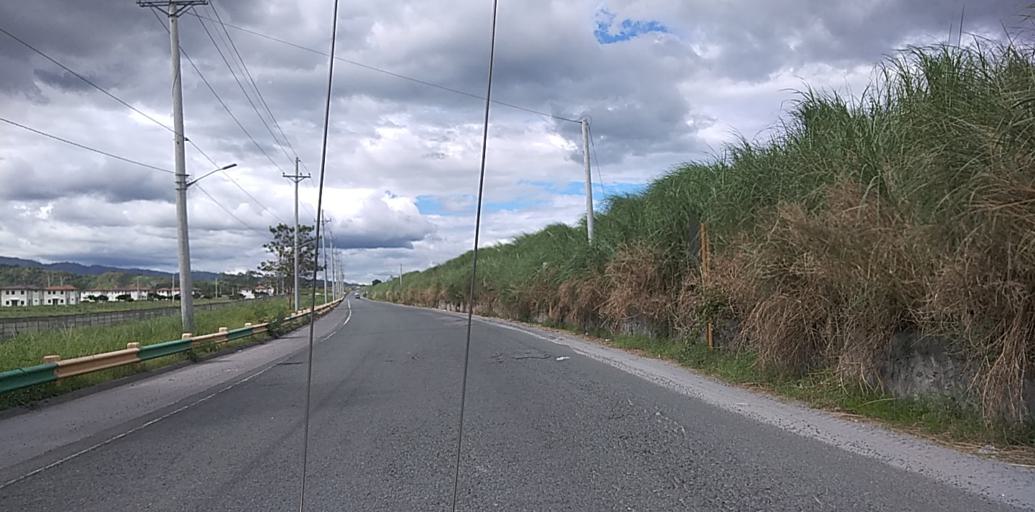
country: PH
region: Central Luzon
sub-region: Province of Pampanga
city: Dolores
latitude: 15.1119
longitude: 120.5176
